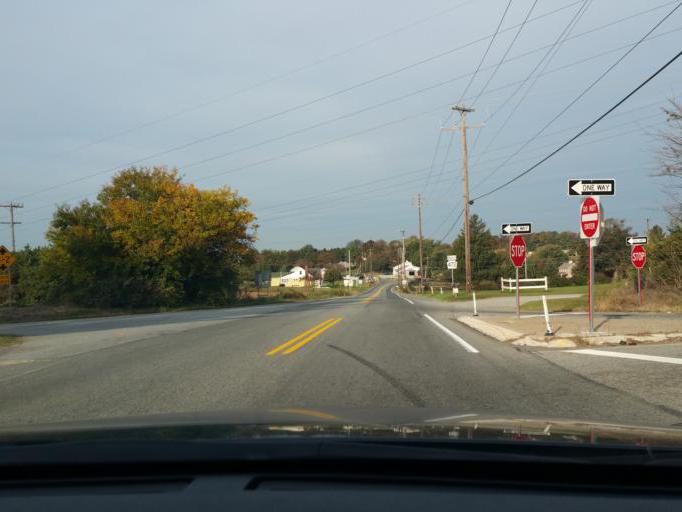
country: US
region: Pennsylvania
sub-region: Chester County
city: Oxford
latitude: 39.7882
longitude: -75.9964
